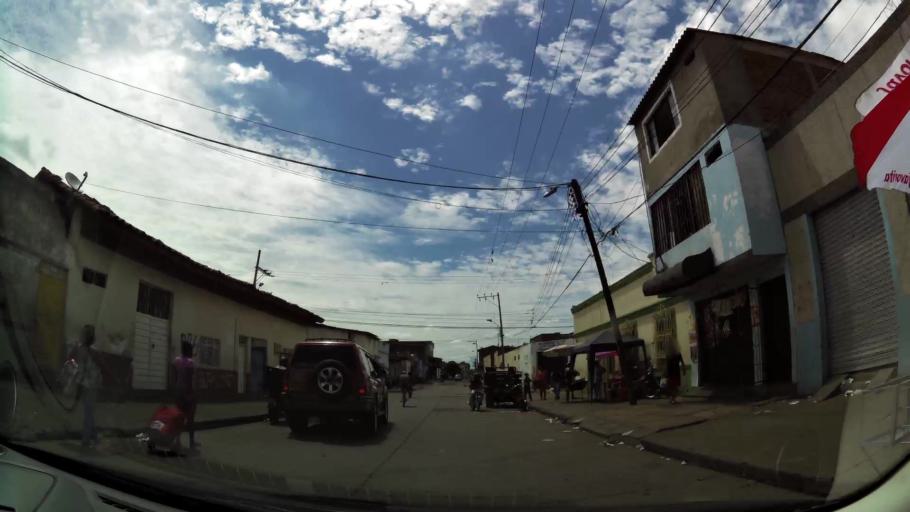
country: CO
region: Valle del Cauca
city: Cali
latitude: 3.4473
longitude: -76.5253
